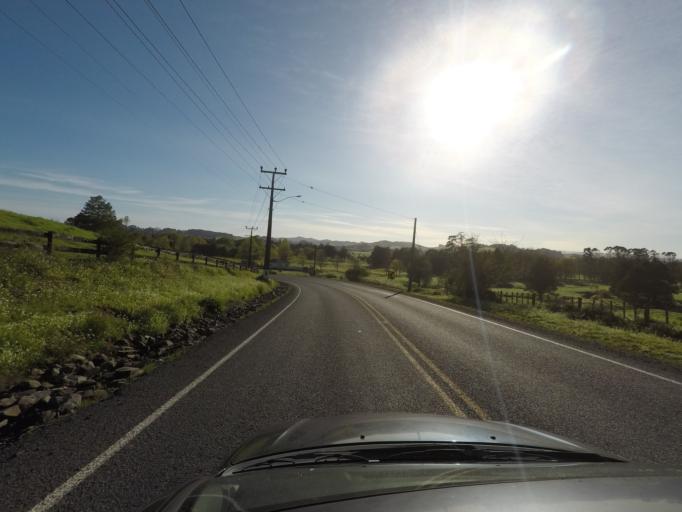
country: NZ
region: Auckland
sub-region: Auckland
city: Red Hill
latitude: -37.0127
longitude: 174.9501
